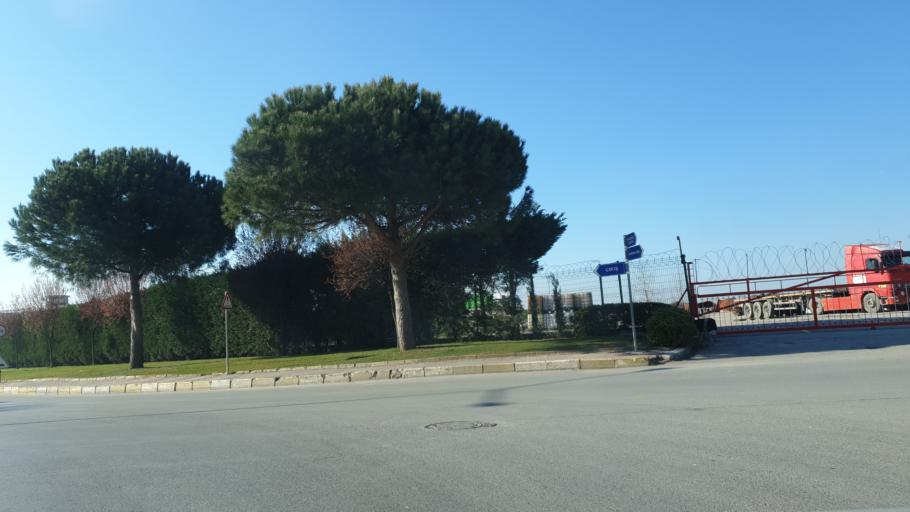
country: TR
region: Istanbul
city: Icmeler
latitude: 40.8812
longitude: 29.3495
